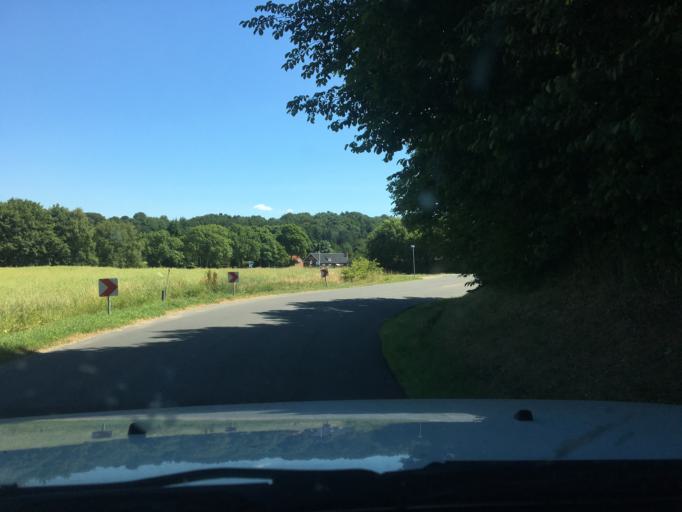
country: DK
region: Central Jutland
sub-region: Horsens Kommune
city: Braedstrup
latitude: 55.9602
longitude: 9.5995
